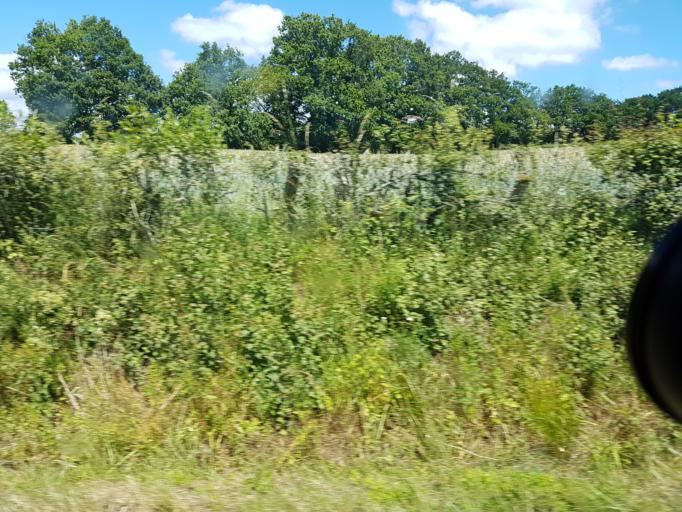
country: FR
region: Bourgogne
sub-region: Departement de Saone-et-Loire
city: Autun
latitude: 47.0565
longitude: 4.2749
